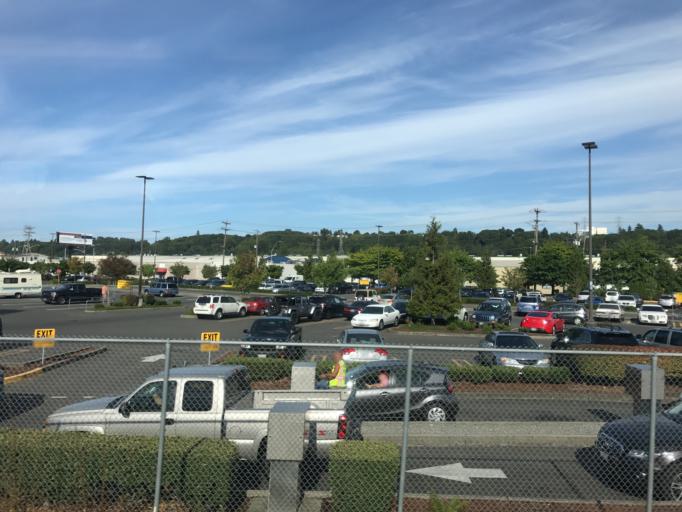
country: US
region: Washington
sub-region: King County
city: Seattle
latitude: 47.5630
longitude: -122.3311
